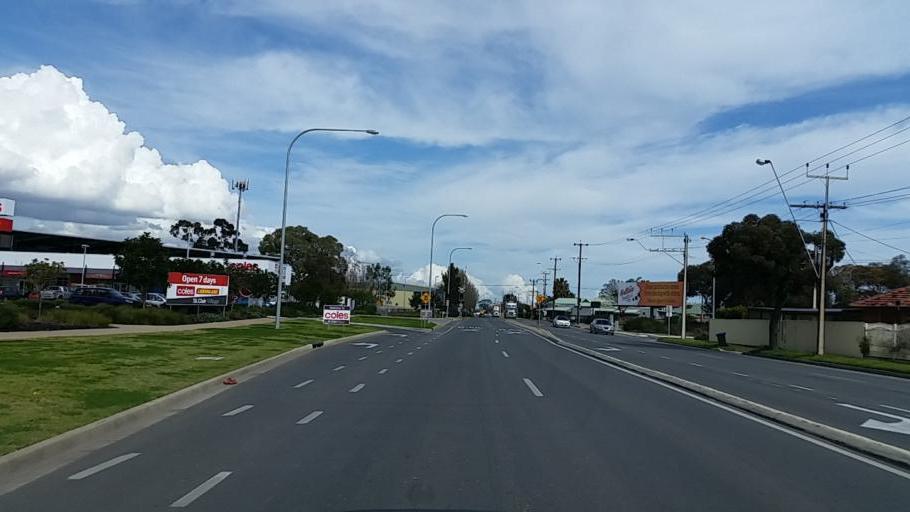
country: AU
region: South Australia
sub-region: Charles Sturt
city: Albert Park
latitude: -34.8686
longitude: 138.5289
